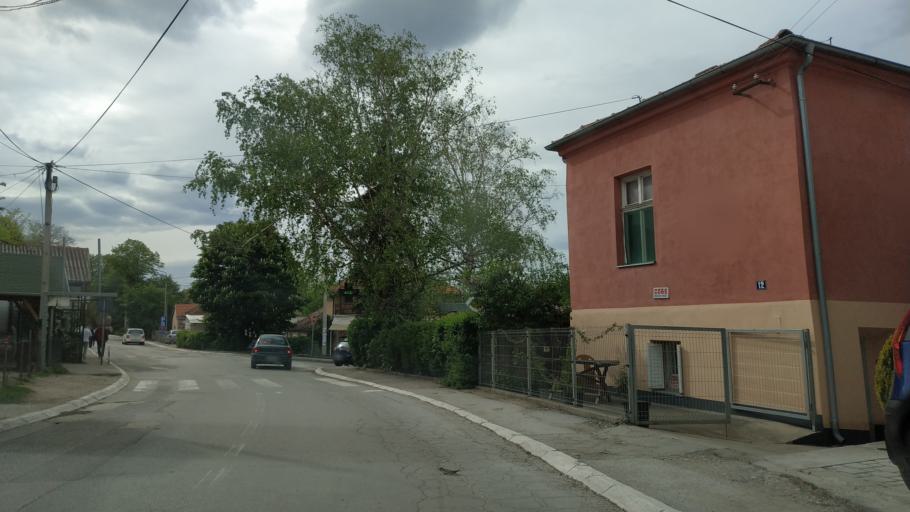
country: RS
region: Central Serbia
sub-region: Zajecarski Okrug
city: Soko Banja
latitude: 43.6452
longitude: 21.8757
